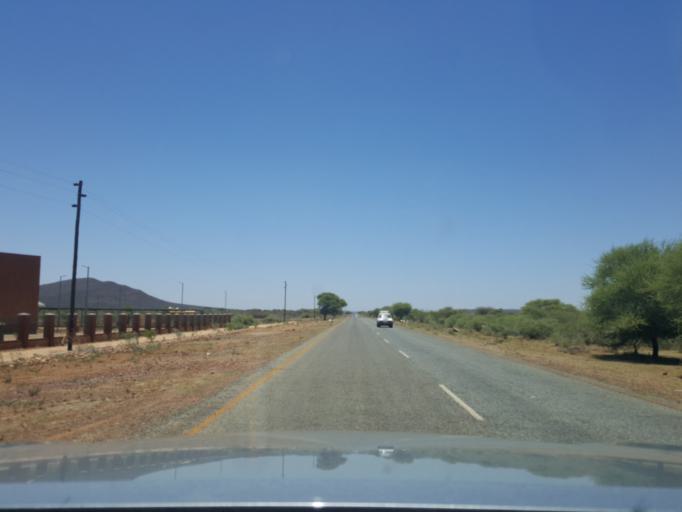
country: BW
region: South East
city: Ramotswa
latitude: -24.9594
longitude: 25.8955
